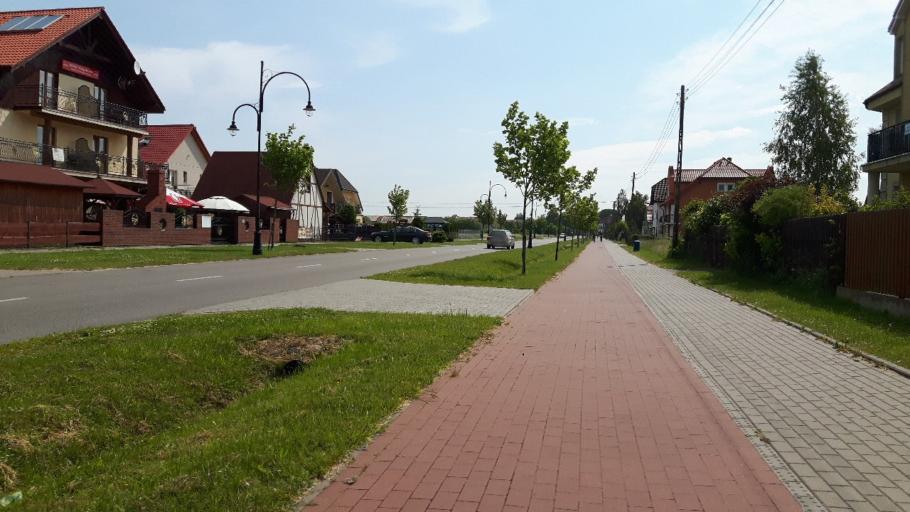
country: PL
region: Pomeranian Voivodeship
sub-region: Powiat leborski
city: Leba
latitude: 54.7502
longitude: 17.5654
